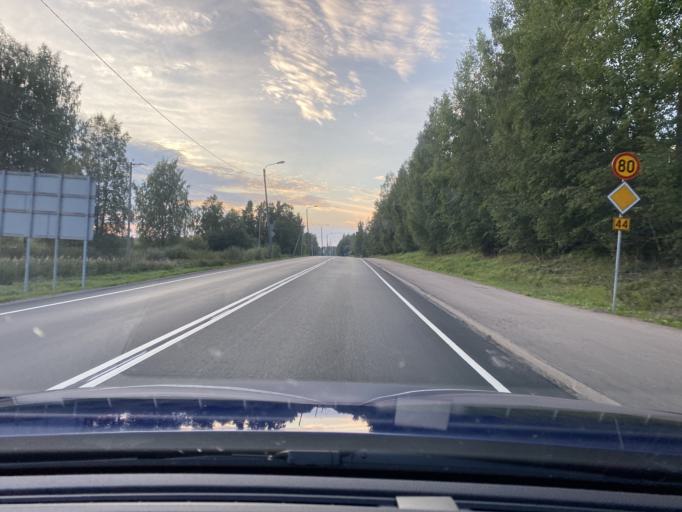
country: FI
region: Satakunta
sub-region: Pohjois-Satakunta
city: Kankaanpaeae
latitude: 61.8195
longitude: 22.3670
